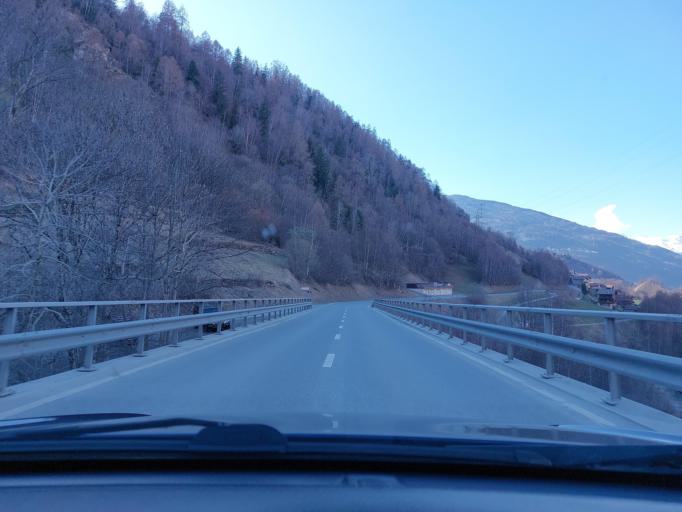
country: CH
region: Valais
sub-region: Herens District
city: Heremence
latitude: 46.1569
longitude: 7.4459
